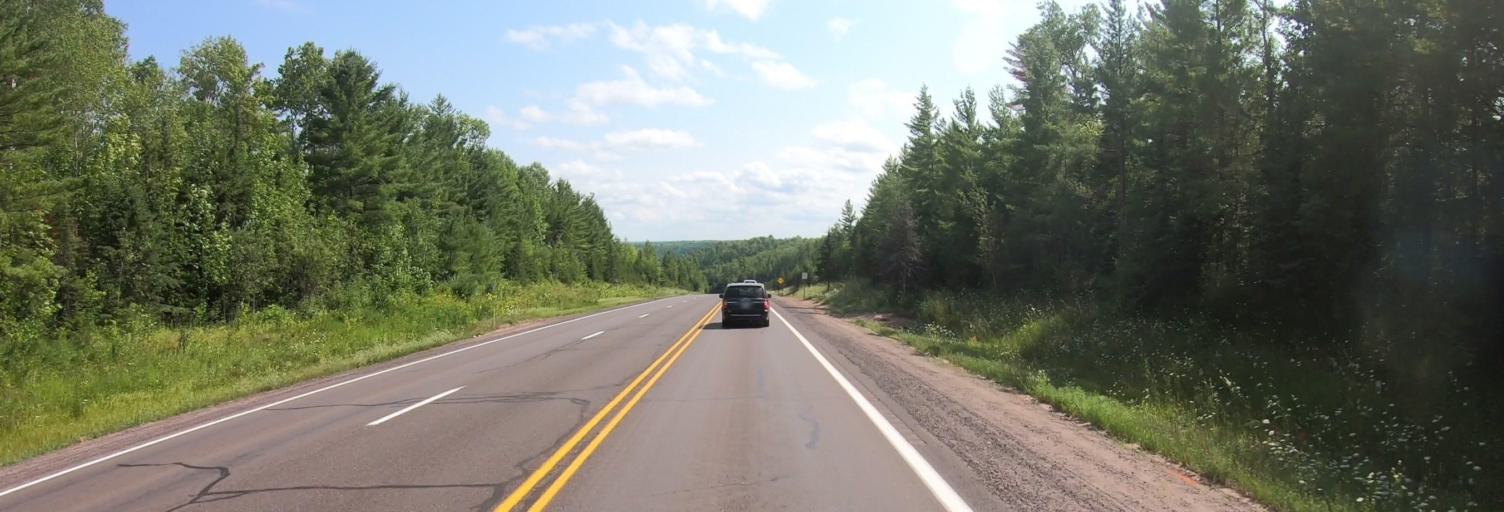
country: US
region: Michigan
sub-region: Ontonagon County
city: Ontonagon
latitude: 46.7127
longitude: -89.1595
